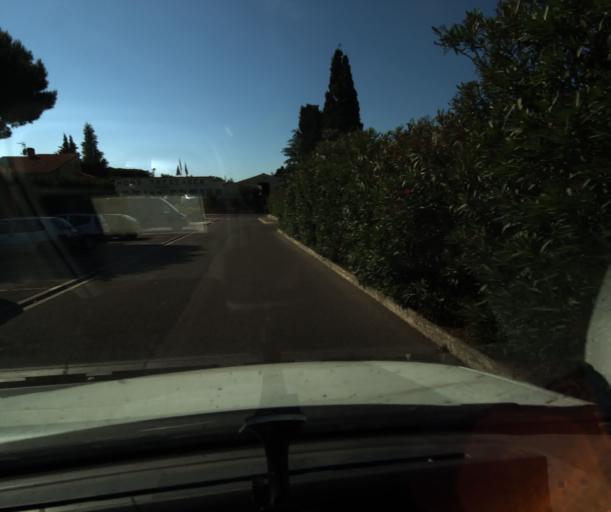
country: FR
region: Languedoc-Roussillon
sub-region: Departement des Pyrenees-Orientales
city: el Volo
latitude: 42.5269
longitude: 2.8358
